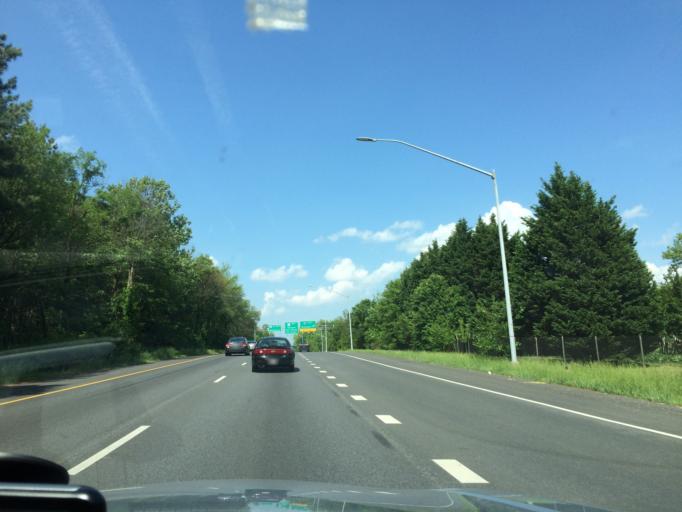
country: US
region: Maryland
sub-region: Anne Arundel County
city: Gambrills
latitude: 39.0600
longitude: -76.6517
